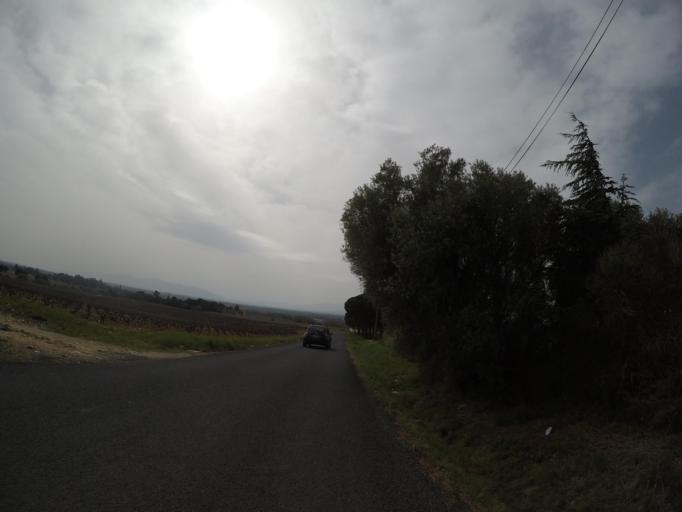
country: FR
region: Languedoc-Roussillon
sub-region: Departement des Pyrenees-Orientales
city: Pezilla-la-Riviere
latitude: 42.7097
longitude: 2.7591
